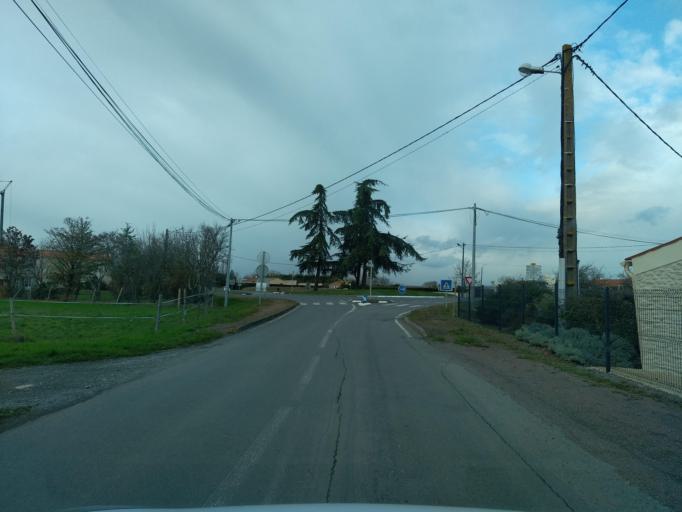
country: FR
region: Pays de la Loire
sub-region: Departement de la Vendee
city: Vix
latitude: 46.3528
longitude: -0.8412
